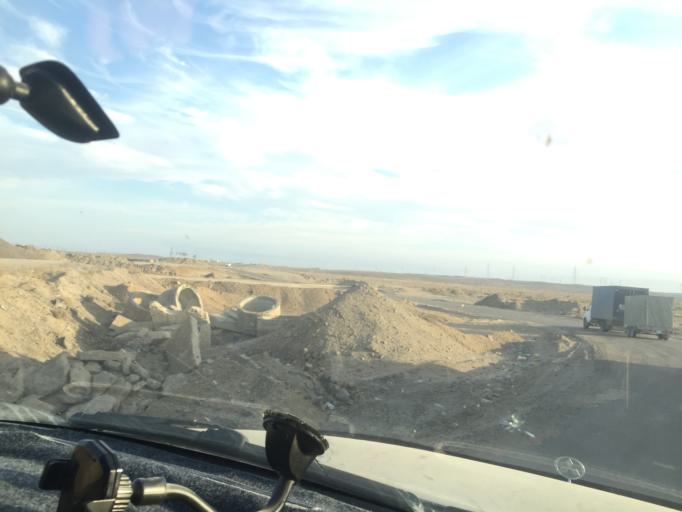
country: KZ
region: Almaty Oblysy
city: Ulken
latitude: 45.2408
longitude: 73.8268
